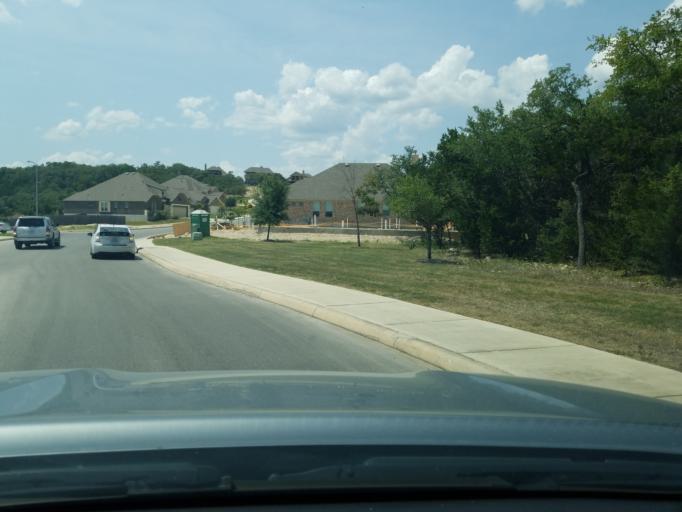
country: US
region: Texas
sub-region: Bexar County
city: Timberwood Park
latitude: 29.6800
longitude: -98.4776
